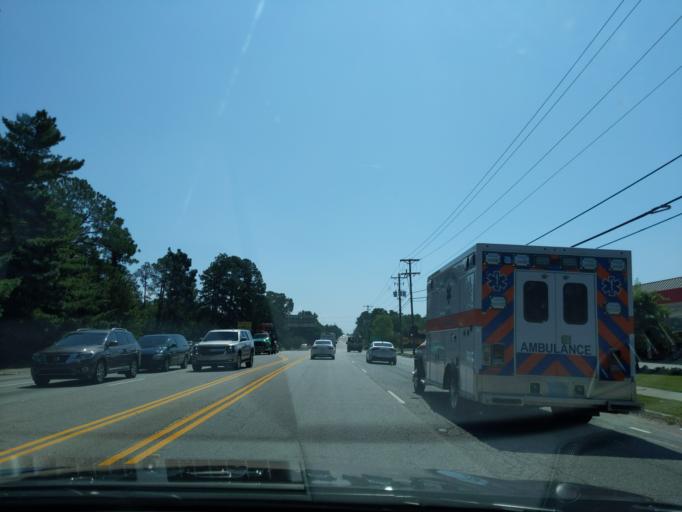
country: US
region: South Carolina
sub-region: Lexington County
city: Lexington
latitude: 33.9779
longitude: -81.1919
